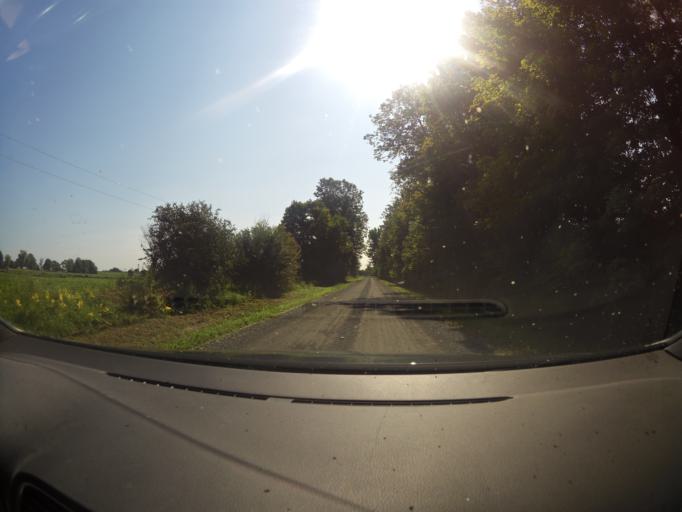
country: CA
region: Ontario
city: Arnprior
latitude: 45.3577
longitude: -76.2641
